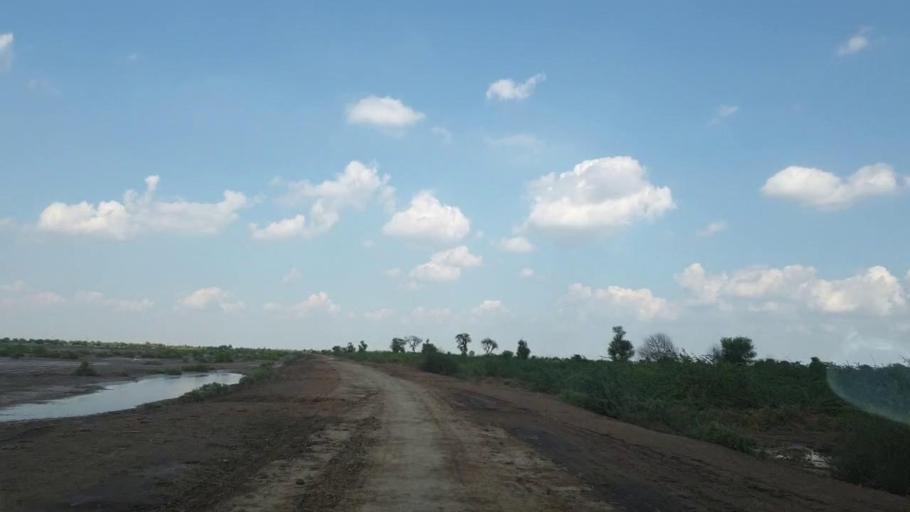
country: PK
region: Sindh
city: Pithoro
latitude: 25.6035
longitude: 69.3700
